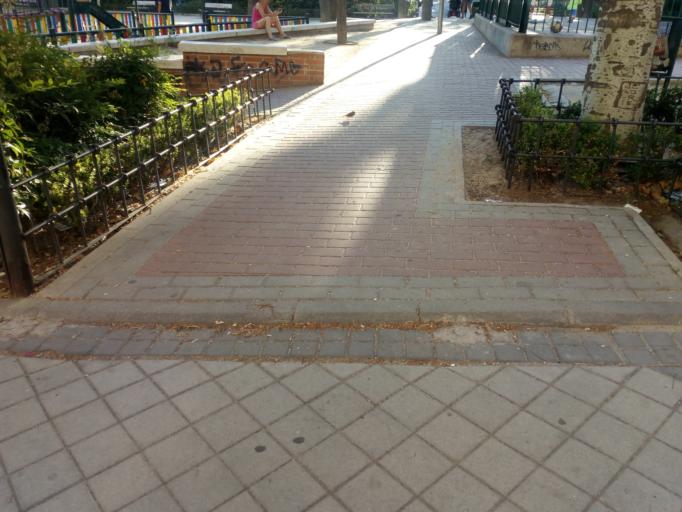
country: ES
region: Madrid
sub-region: Provincia de Madrid
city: Retiro
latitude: 40.4095
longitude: -3.6713
